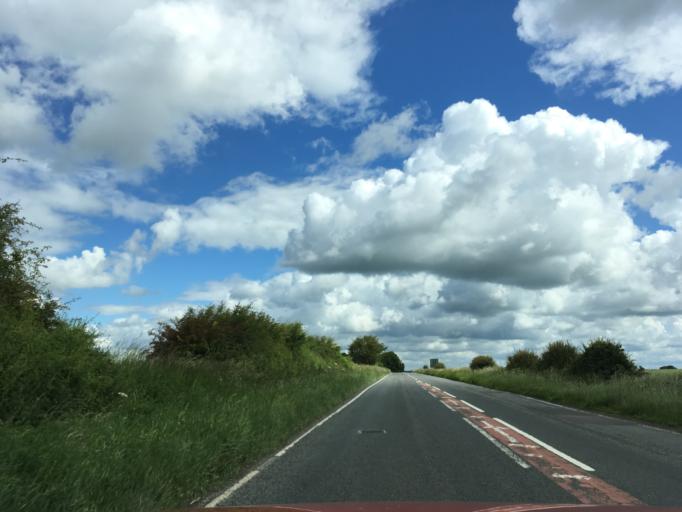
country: GB
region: England
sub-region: Oxfordshire
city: Shipton under Wychwood
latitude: 51.8382
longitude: -1.6048
